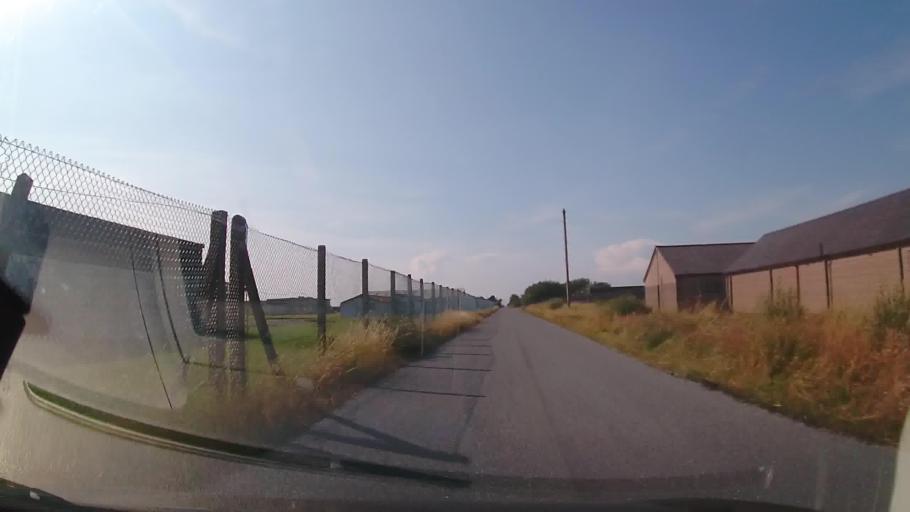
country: GB
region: Wales
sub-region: Gwynedd
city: Llanbedr
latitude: 52.8178
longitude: -4.1184
